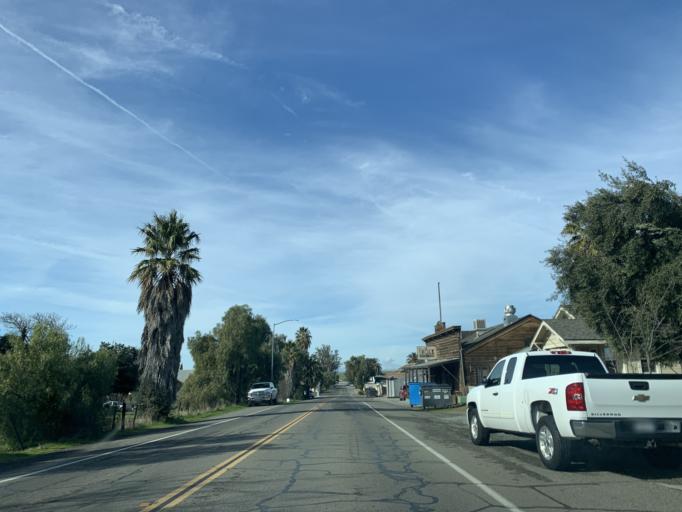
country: US
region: California
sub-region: San Benito County
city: Ridgemark
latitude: 36.7884
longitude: -121.3181
